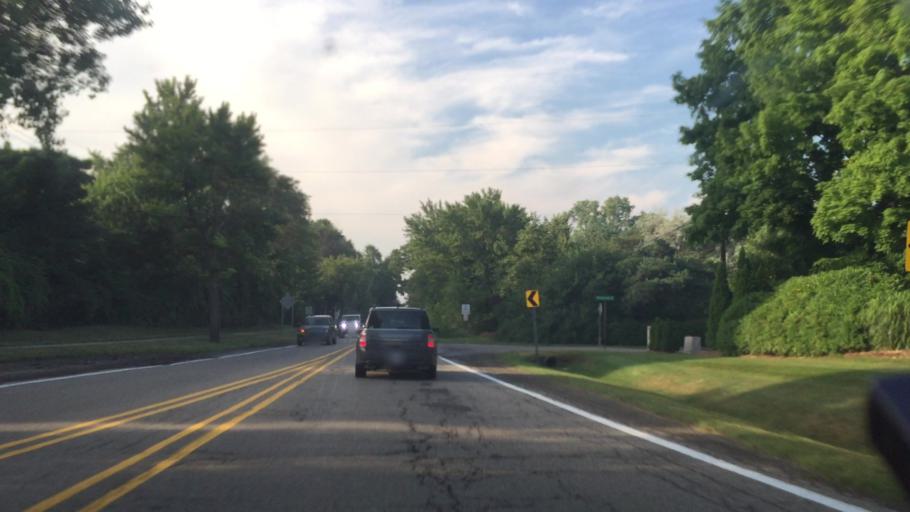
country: US
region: Michigan
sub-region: Oakland County
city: Bloomfield Hills
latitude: 42.6033
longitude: -83.2479
